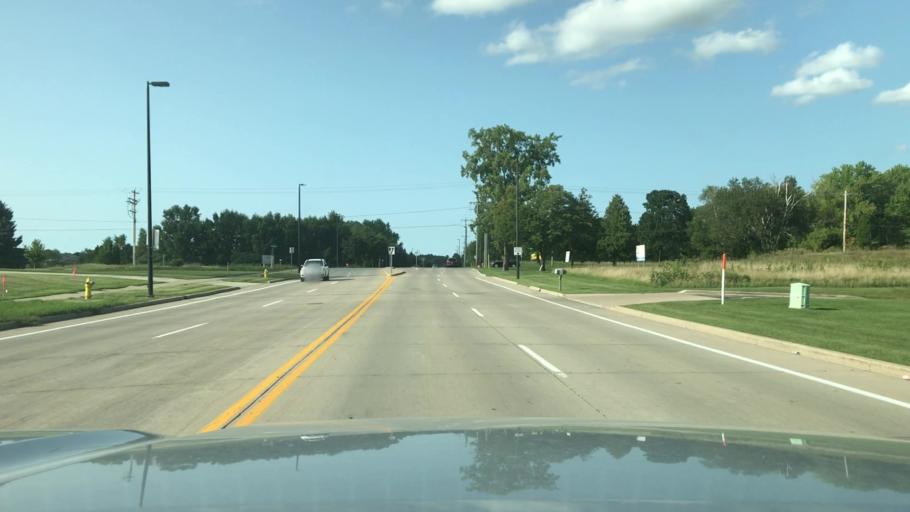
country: US
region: Wisconsin
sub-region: Brown County
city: Bellevue
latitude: 44.4868
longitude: -87.9178
